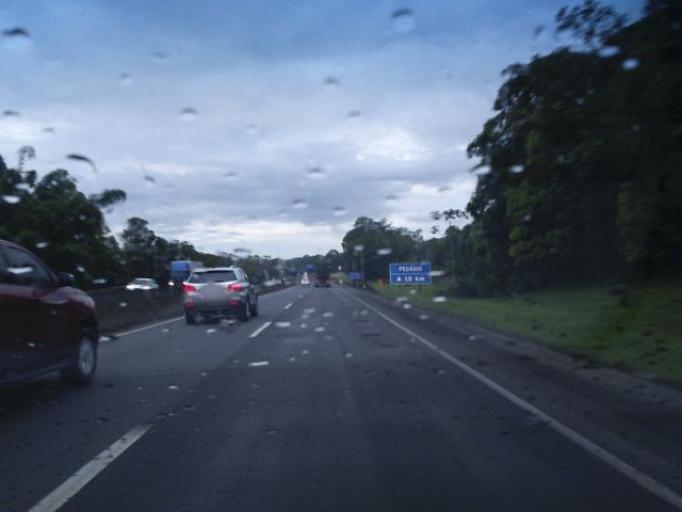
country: BR
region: Parana
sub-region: Guaratuba
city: Guaratuba
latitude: -25.9764
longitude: -48.8891
